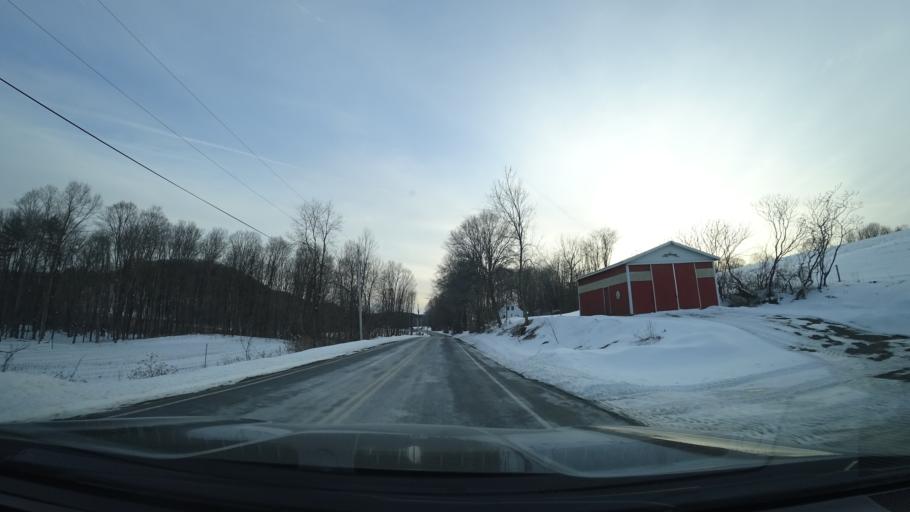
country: US
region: New York
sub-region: Washington County
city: Fort Edward
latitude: 43.2474
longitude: -73.4303
